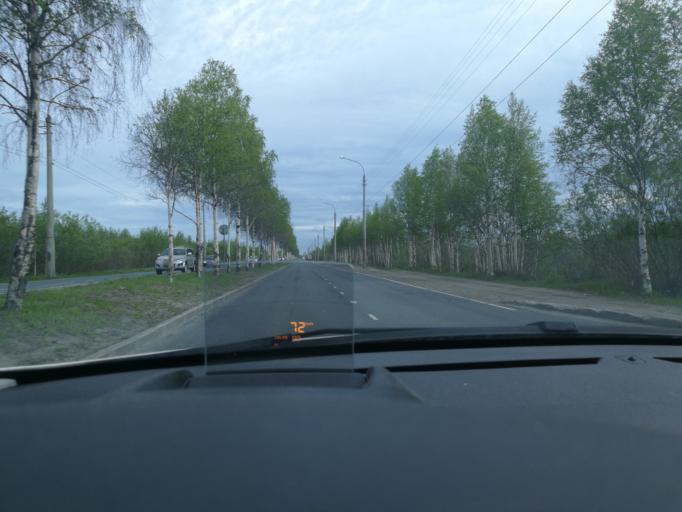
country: RU
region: Arkhangelskaya
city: Arkhangel'sk
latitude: 64.6122
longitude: 40.5251
